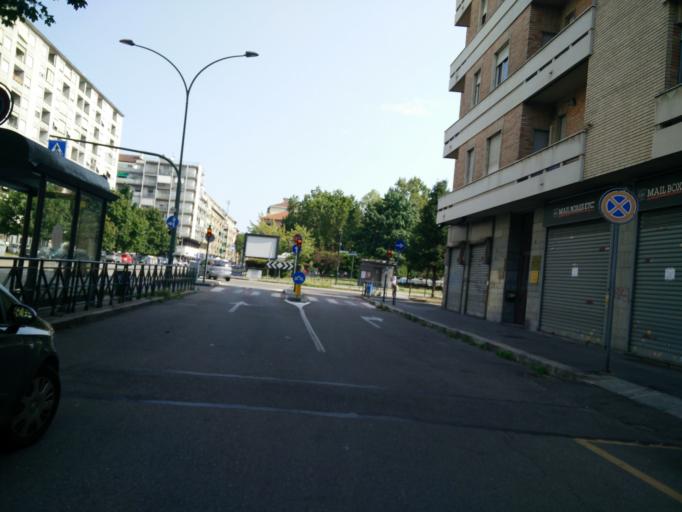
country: IT
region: Piedmont
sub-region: Provincia di Torino
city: Lesna
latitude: 45.0327
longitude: 7.6531
